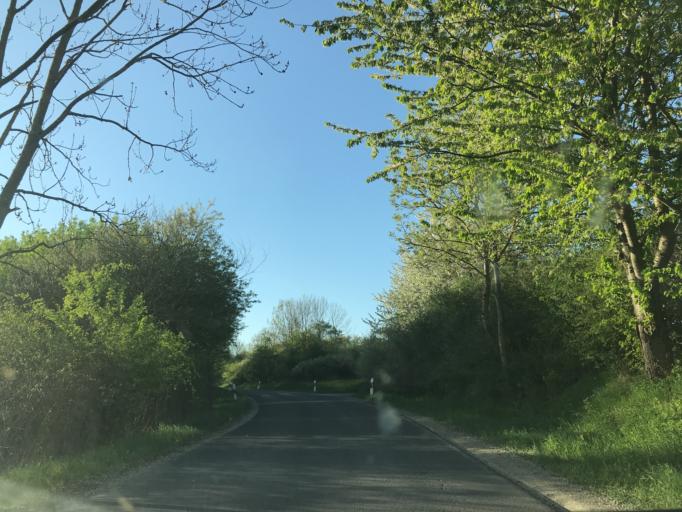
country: DE
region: Thuringia
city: Heuthen
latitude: 51.3389
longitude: 10.2374
